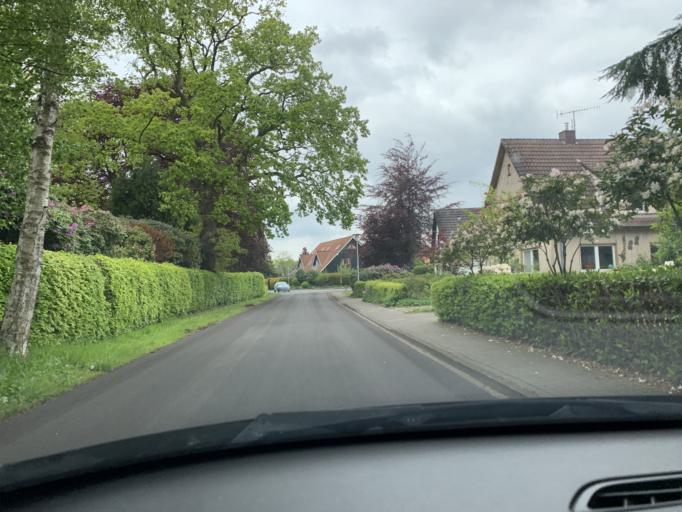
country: DE
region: Lower Saxony
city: Westerstede
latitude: 53.2484
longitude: 7.9128
